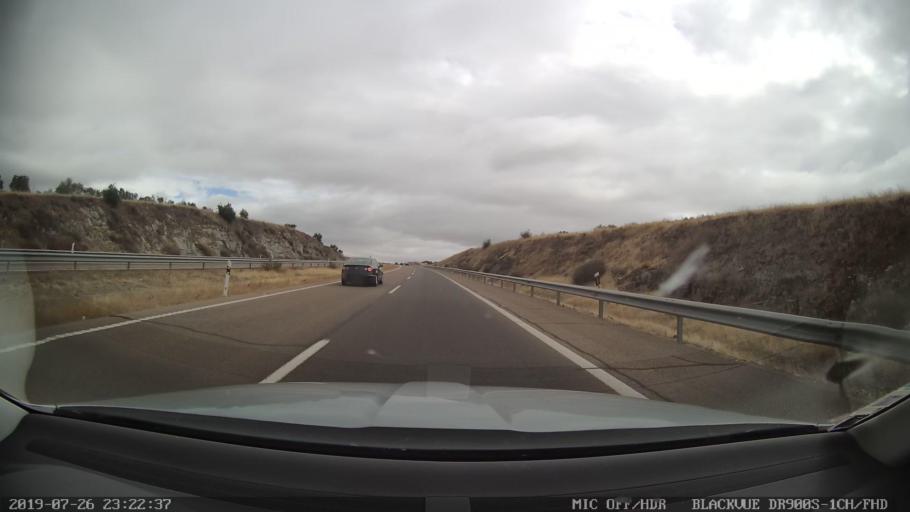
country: ES
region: Extremadura
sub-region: Provincia de Caceres
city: Miajadas
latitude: 39.1465
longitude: -5.9323
